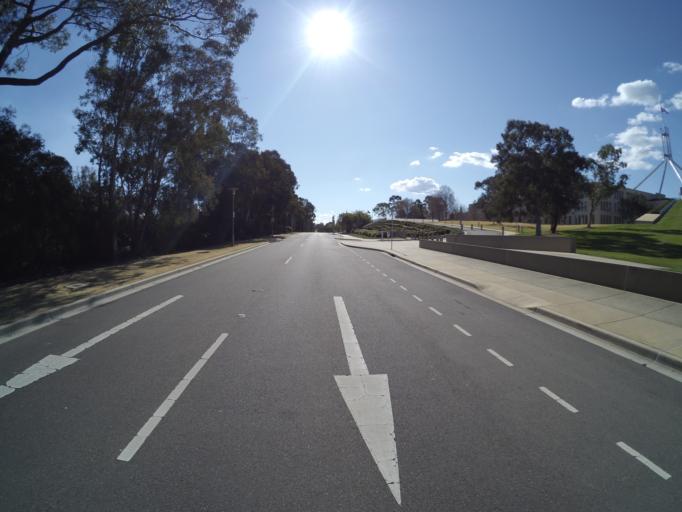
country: AU
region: Australian Capital Territory
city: Forrest
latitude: -35.3106
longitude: 149.1239
